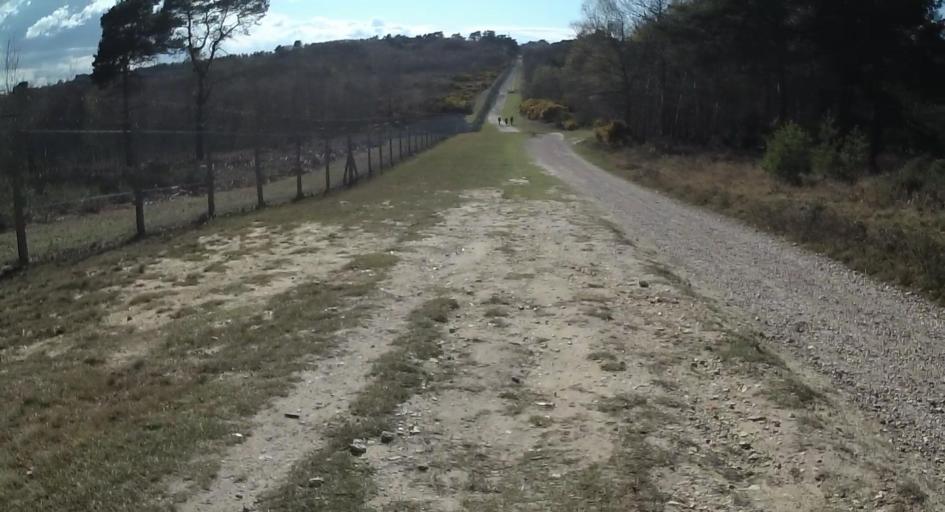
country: GB
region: England
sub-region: Surrey
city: Bagshot
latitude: 51.3384
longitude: -0.6890
